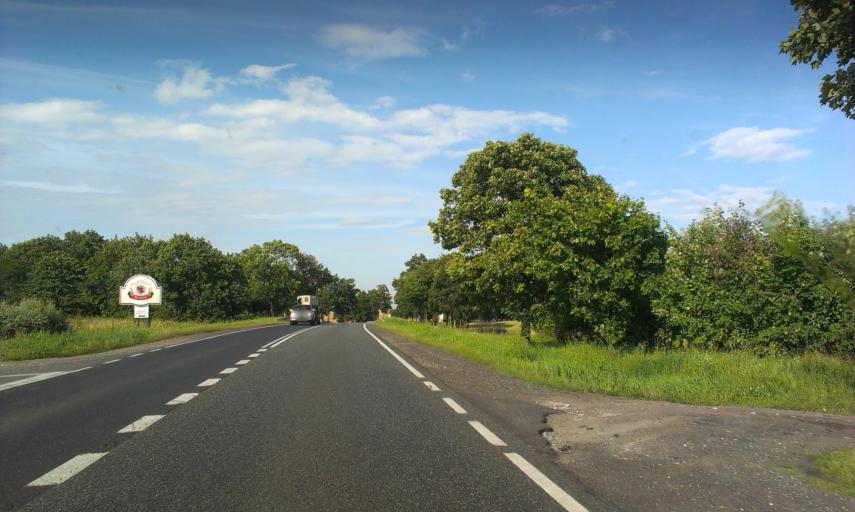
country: PL
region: Kujawsko-Pomorskie
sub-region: Powiat nakielski
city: Naklo nad Notecia
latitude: 53.1569
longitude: 17.6234
